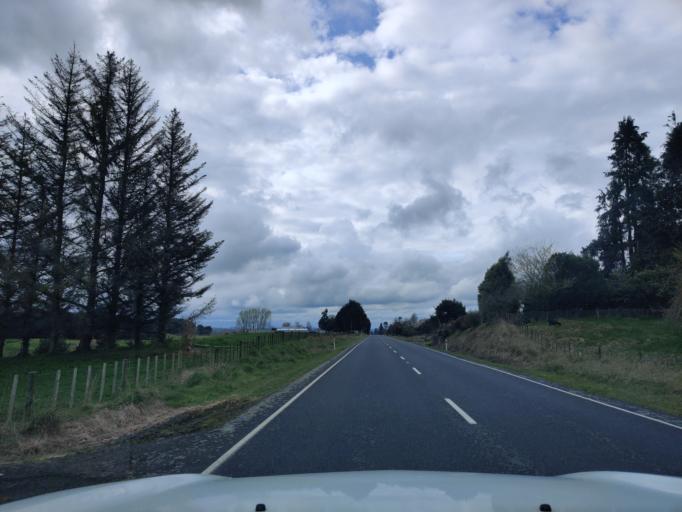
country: NZ
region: Waikato
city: Turangi
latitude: -39.0439
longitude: 175.3833
